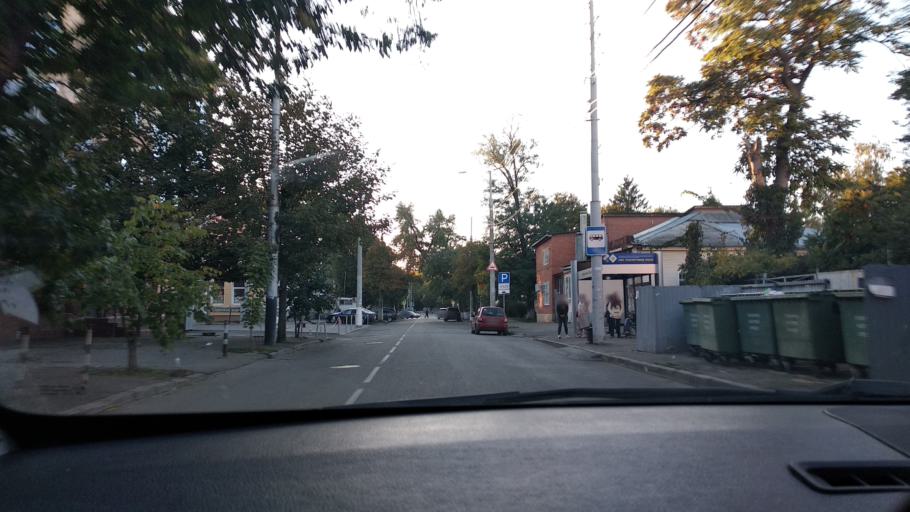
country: RU
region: Krasnodarskiy
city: Krasnodar
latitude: 45.0153
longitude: 38.9735
